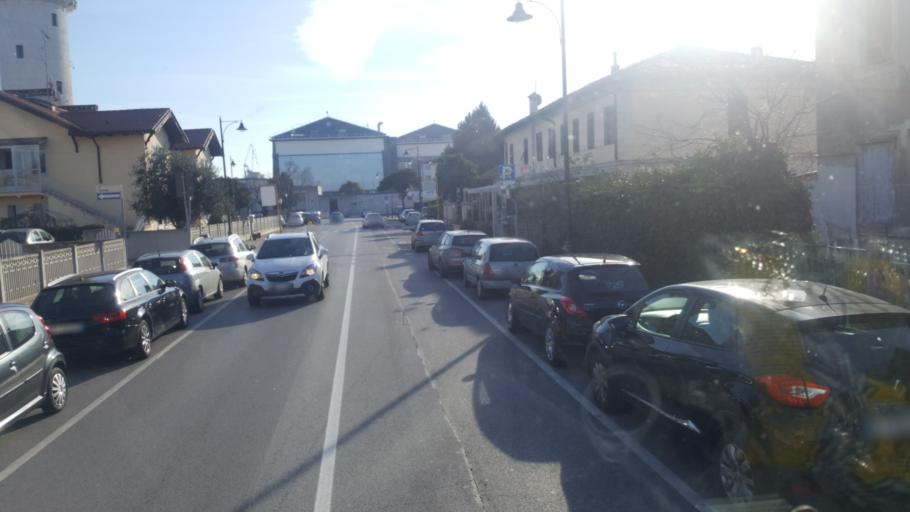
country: IT
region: Friuli Venezia Giulia
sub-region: Provincia di Gorizia
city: Monfalcone
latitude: 45.7976
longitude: 13.5354
